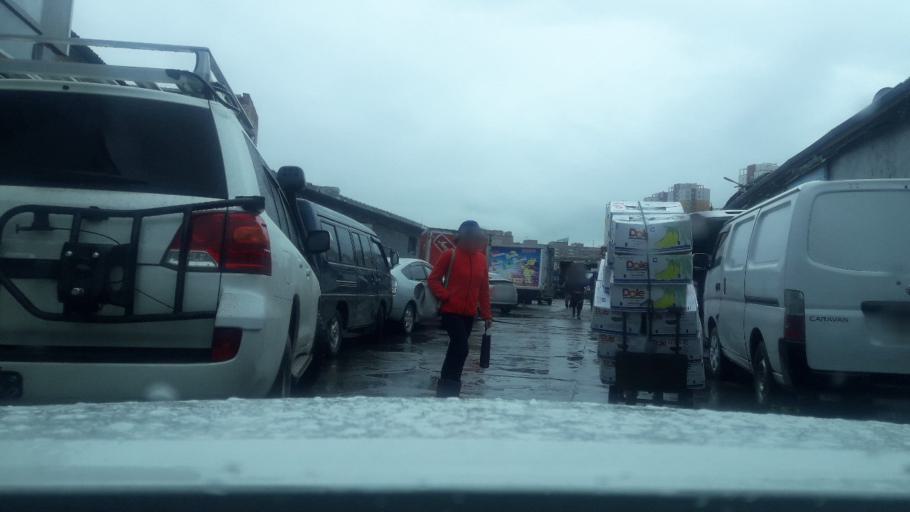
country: MN
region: Ulaanbaatar
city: Ulaanbaatar
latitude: 47.9087
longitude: 106.8909
